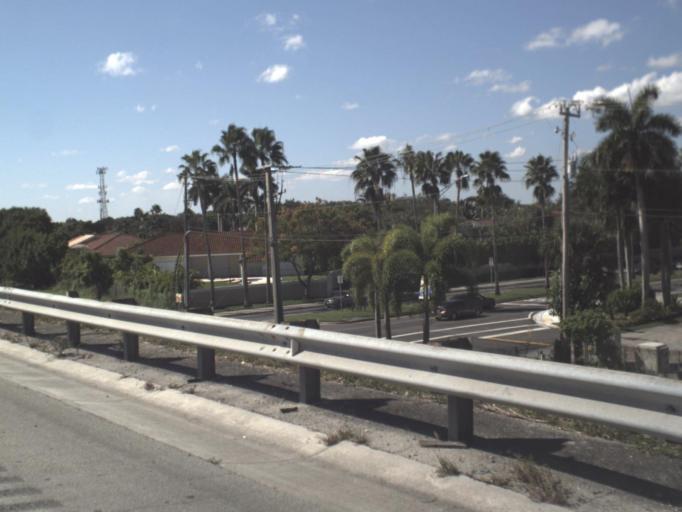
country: US
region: Florida
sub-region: Miami-Dade County
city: Kendale Lakes
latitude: 25.7015
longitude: -80.3838
